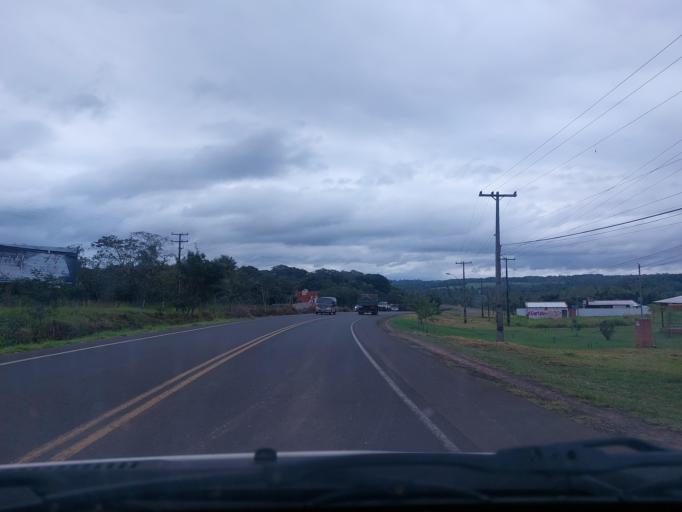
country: PY
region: San Pedro
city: Guayaybi
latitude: -24.6698
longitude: -56.4120
